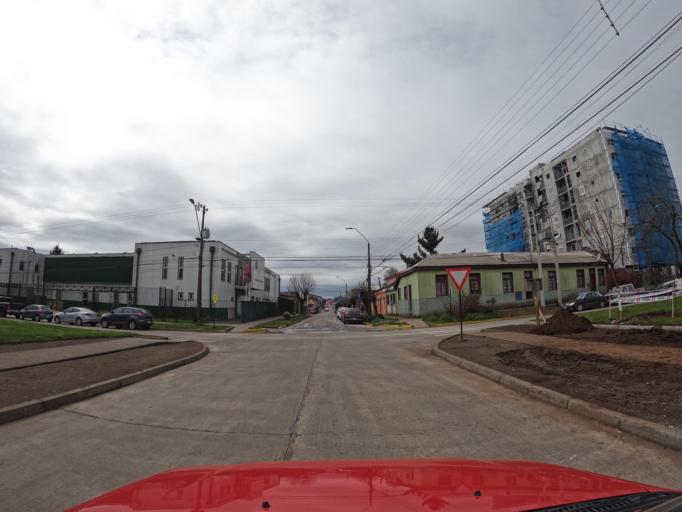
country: CL
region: Araucania
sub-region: Provincia de Malleco
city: Victoria
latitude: -38.2367
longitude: -72.3363
